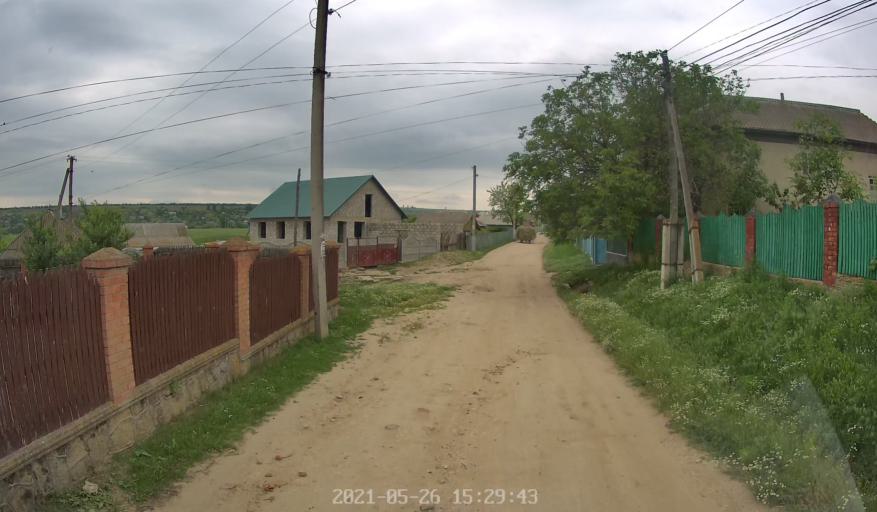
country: MD
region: Hincesti
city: Dancu
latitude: 46.6683
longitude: 28.3197
